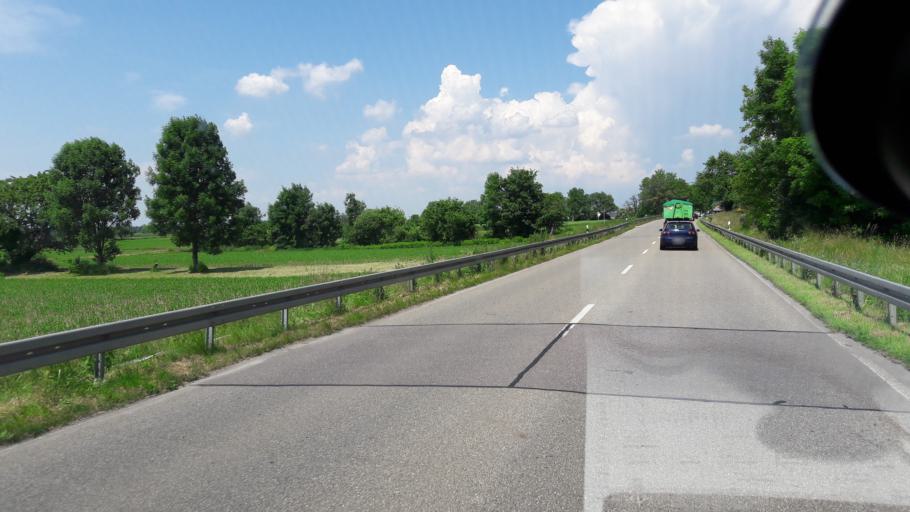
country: DE
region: Baden-Wuerttemberg
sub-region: Karlsruhe Region
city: Weingarten
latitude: 49.0383
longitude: 8.5214
